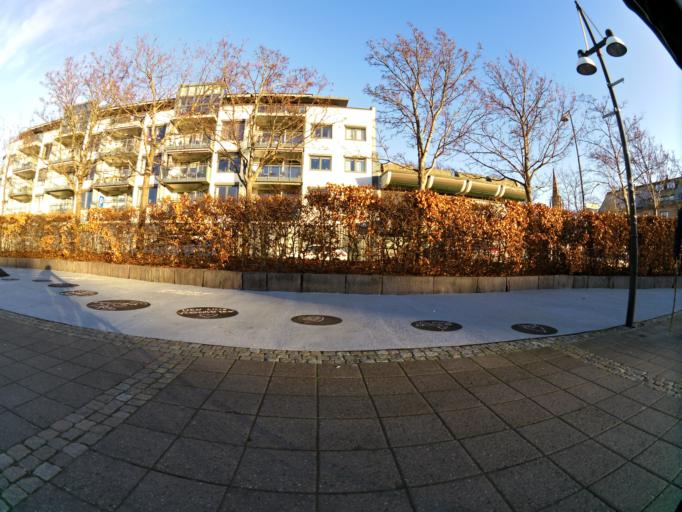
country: NO
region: Ostfold
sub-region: Fredrikstad
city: Fredrikstad
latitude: 59.2100
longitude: 10.9385
